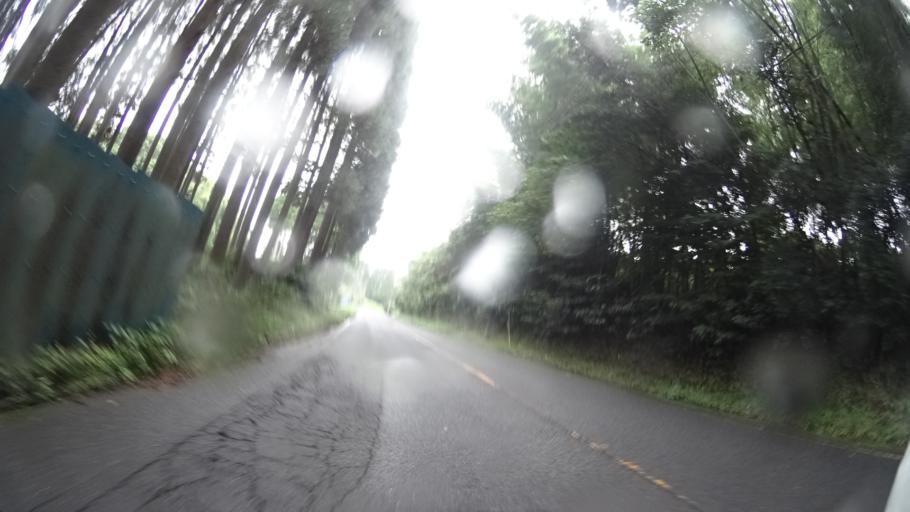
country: JP
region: Kagoshima
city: Kajiki
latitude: 31.7837
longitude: 130.6742
